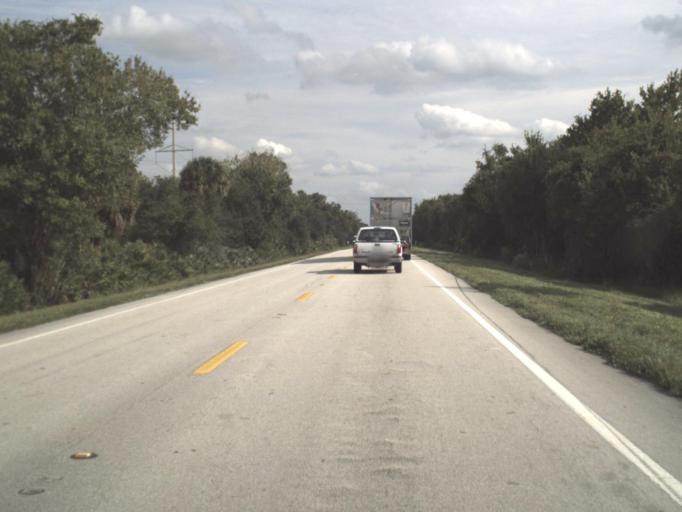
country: US
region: Florida
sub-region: Okeechobee County
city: Taylor Creek
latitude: 27.1777
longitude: -80.7056
